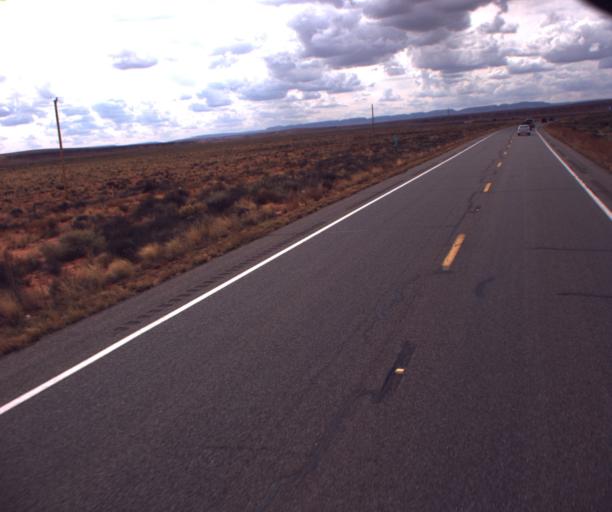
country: US
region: Arizona
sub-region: Navajo County
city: Kayenta
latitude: 36.7885
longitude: -109.9534
